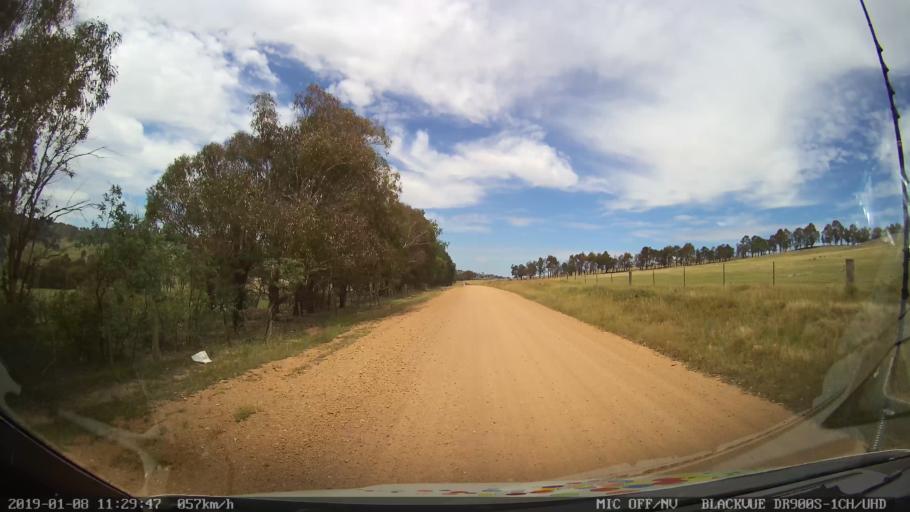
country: AU
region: New South Wales
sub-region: Guyra
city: Guyra
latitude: -30.3029
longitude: 151.5472
